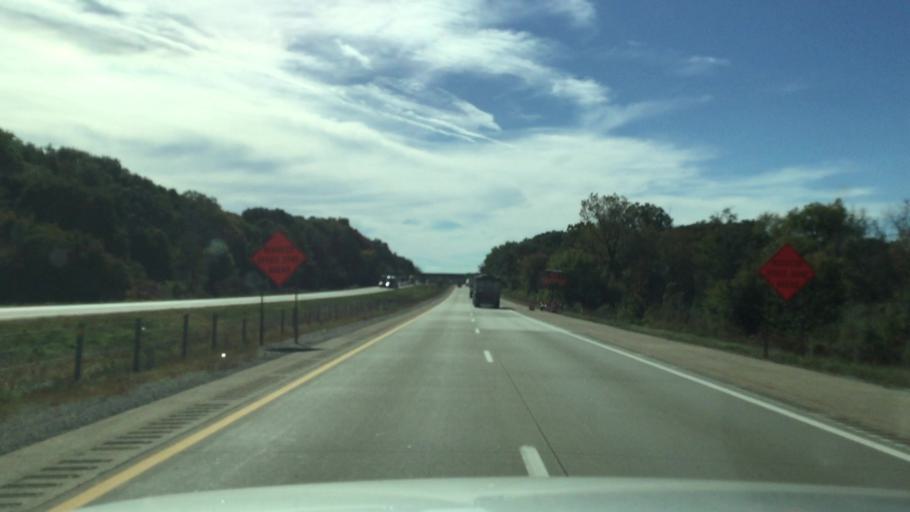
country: US
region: Michigan
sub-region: Jackson County
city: Michigan Center
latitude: 42.2872
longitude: -84.2781
